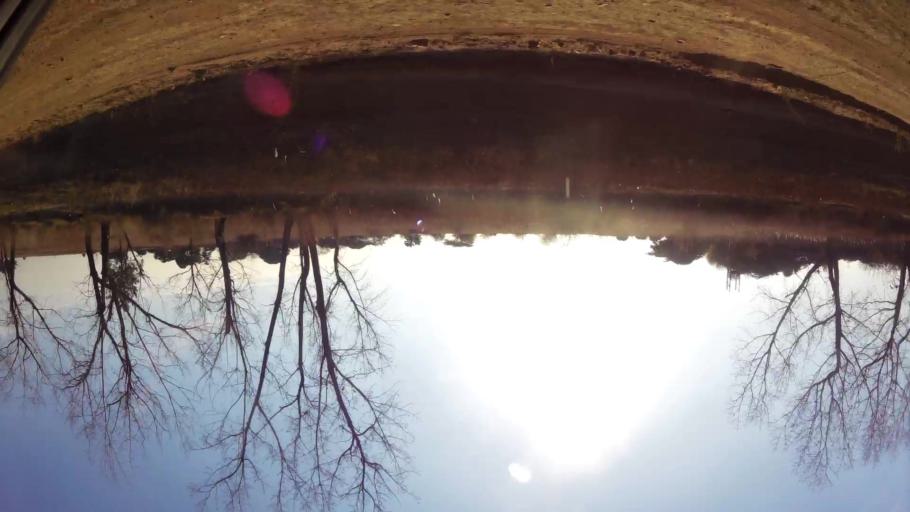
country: ZA
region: Gauteng
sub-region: City of Johannesburg Metropolitan Municipality
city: Diepsloot
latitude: -25.9767
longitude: 27.9459
